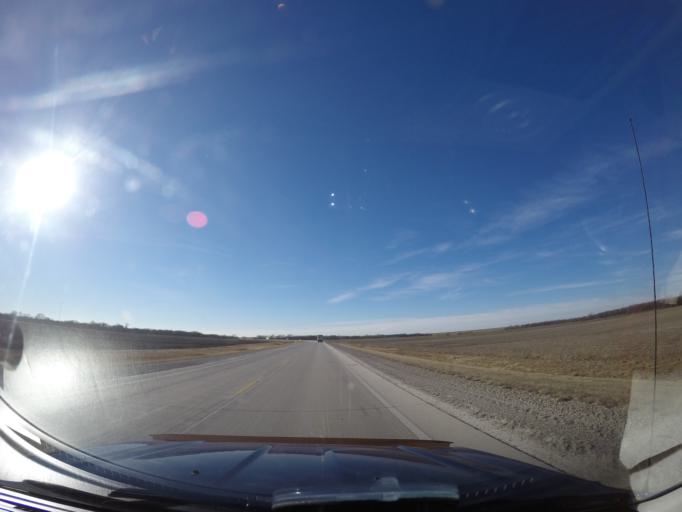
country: US
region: Kansas
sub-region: Marion County
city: Marion
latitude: 38.3629
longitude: -97.0594
